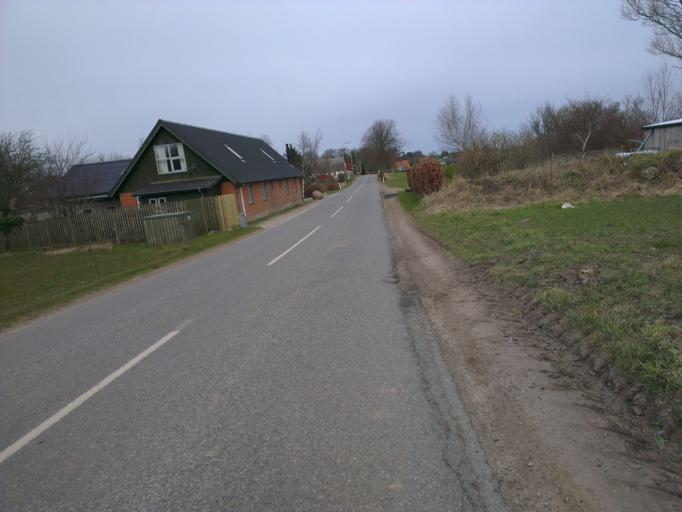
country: DK
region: Capital Region
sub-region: Frederikssund Kommune
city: Skibby
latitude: 55.7909
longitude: 11.9193
